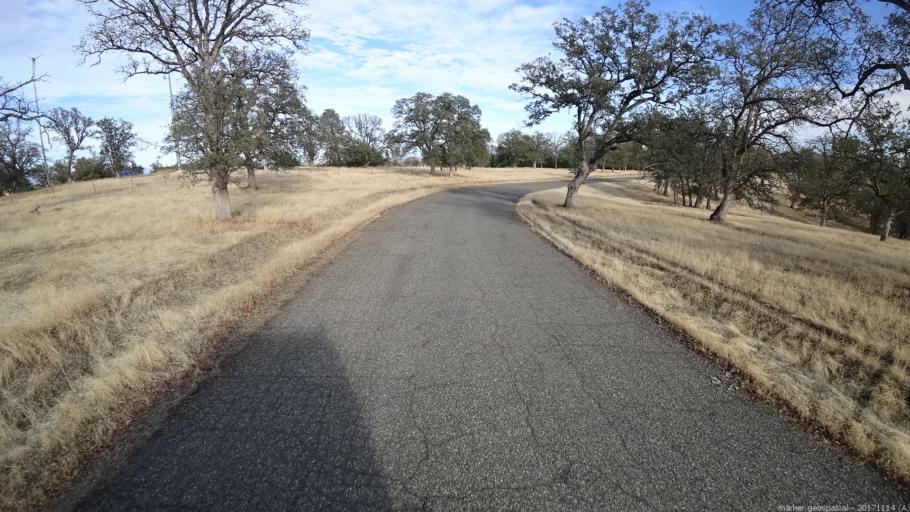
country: US
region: California
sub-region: Shasta County
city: Shasta
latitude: 40.3837
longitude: -122.5868
